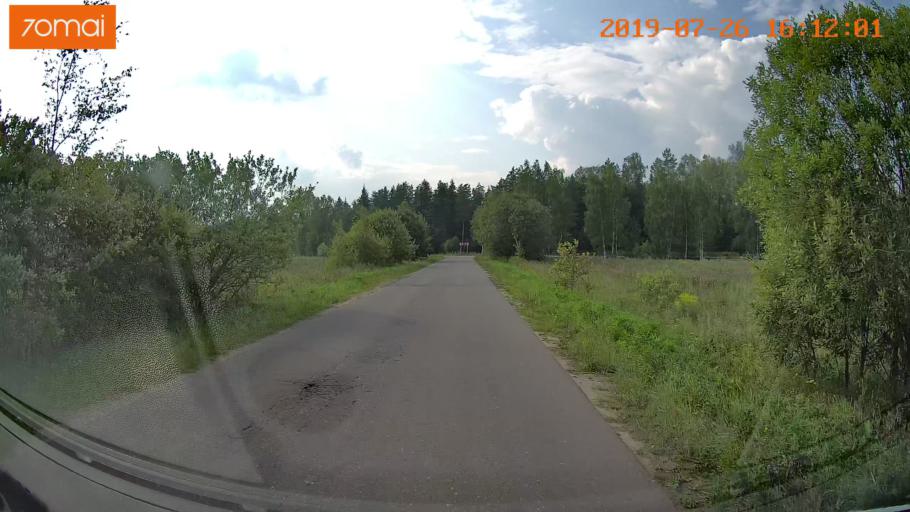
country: RU
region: Ivanovo
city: Bogorodskoye
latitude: 57.0680
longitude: 41.0518
